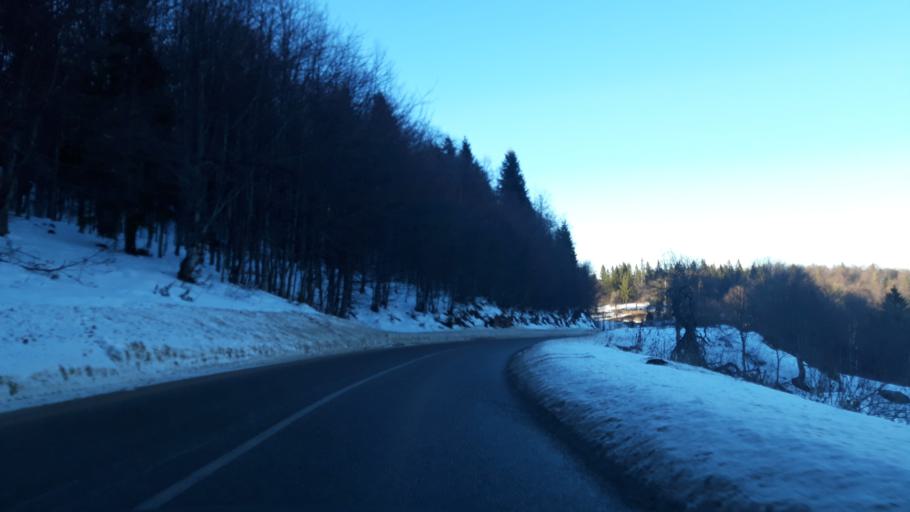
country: BA
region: Republika Srpska
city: Vlasenica
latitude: 44.1426
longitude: 18.9444
